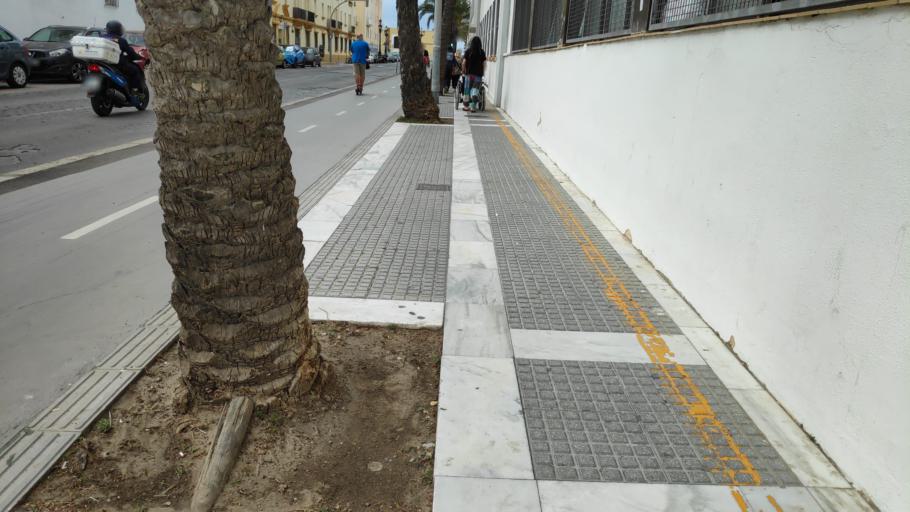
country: ES
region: Andalusia
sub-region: Provincia de Cadiz
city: Cadiz
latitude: 36.5298
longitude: -6.3053
